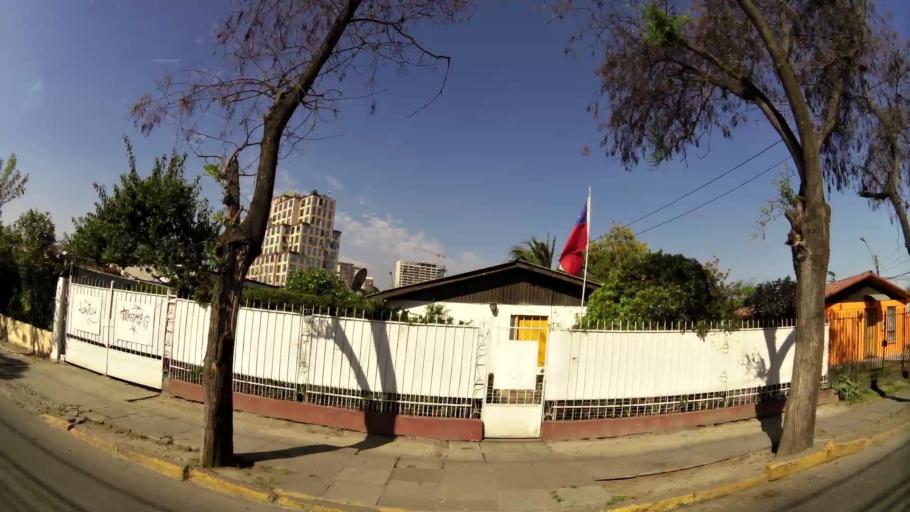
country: CL
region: Santiago Metropolitan
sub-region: Provincia de Santiago
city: Villa Presidente Frei, Nunoa, Santiago, Chile
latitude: -33.5217
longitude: -70.6030
